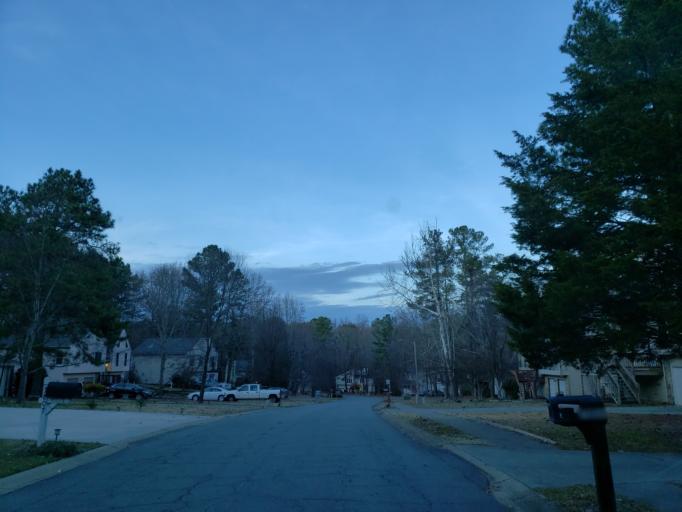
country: US
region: Georgia
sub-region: Cobb County
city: Kennesaw
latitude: 34.0466
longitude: -84.6451
